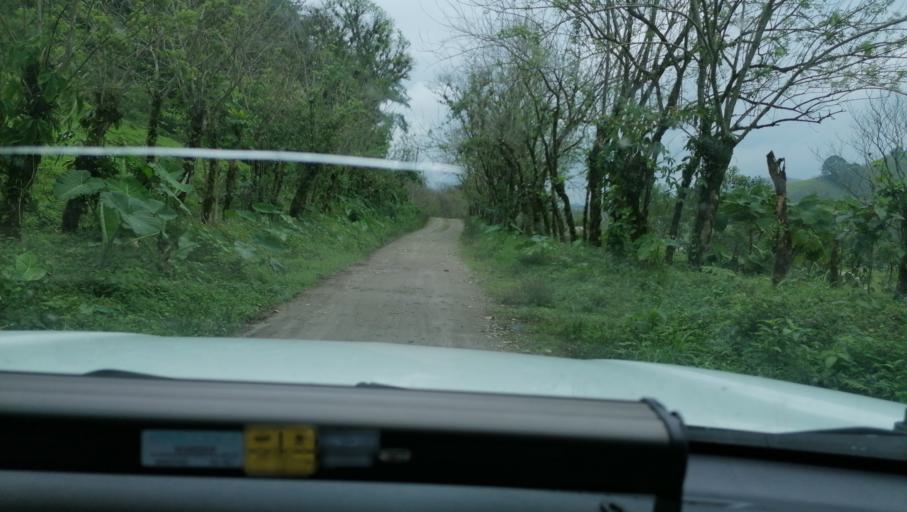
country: MX
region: Chiapas
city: Ixtacomitan
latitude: 17.3523
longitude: -93.1609
